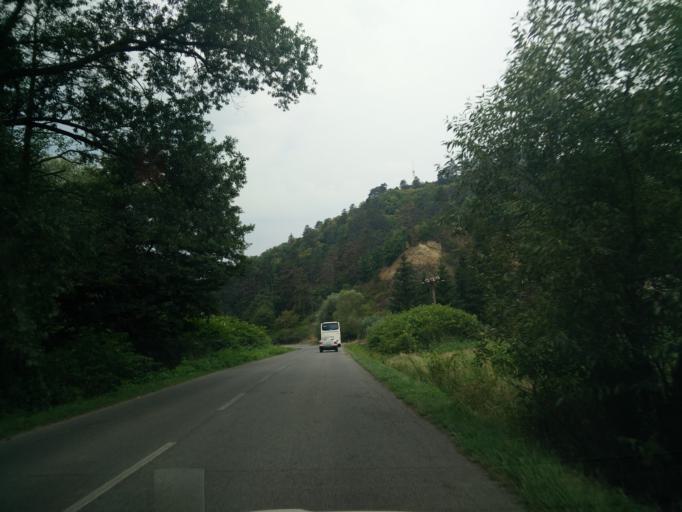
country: SK
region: Banskobystricky
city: Ziar nad Hronom
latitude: 48.5918
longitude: 18.8800
